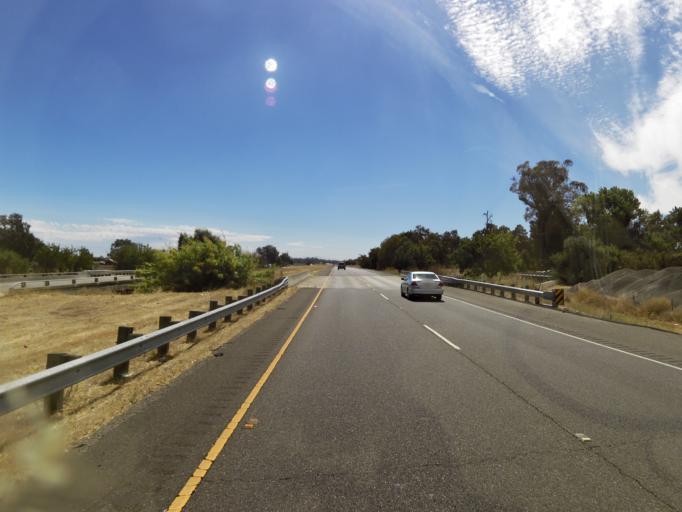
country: US
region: California
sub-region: Solano County
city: Allendale
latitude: 38.4486
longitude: -121.9425
